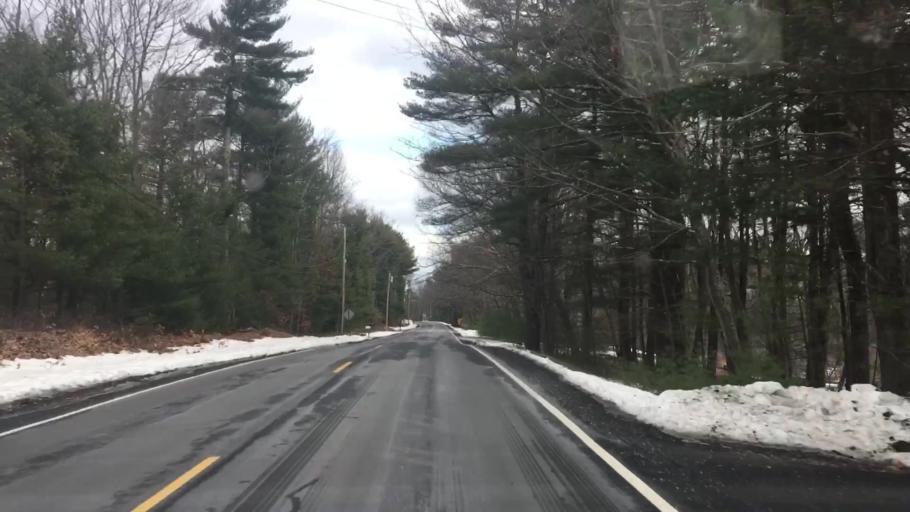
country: US
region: Maine
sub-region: York County
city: Wells Beach Station
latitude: 43.3273
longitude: -70.6290
